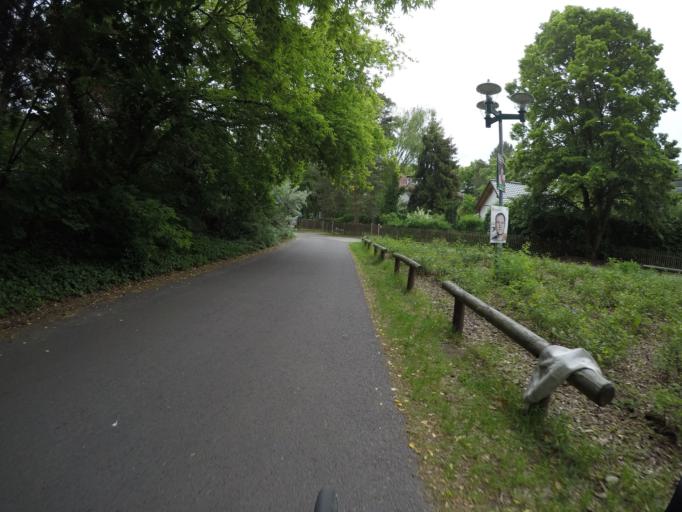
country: DE
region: Brandenburg
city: Glienicke
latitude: 52.6285
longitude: 13.3302
